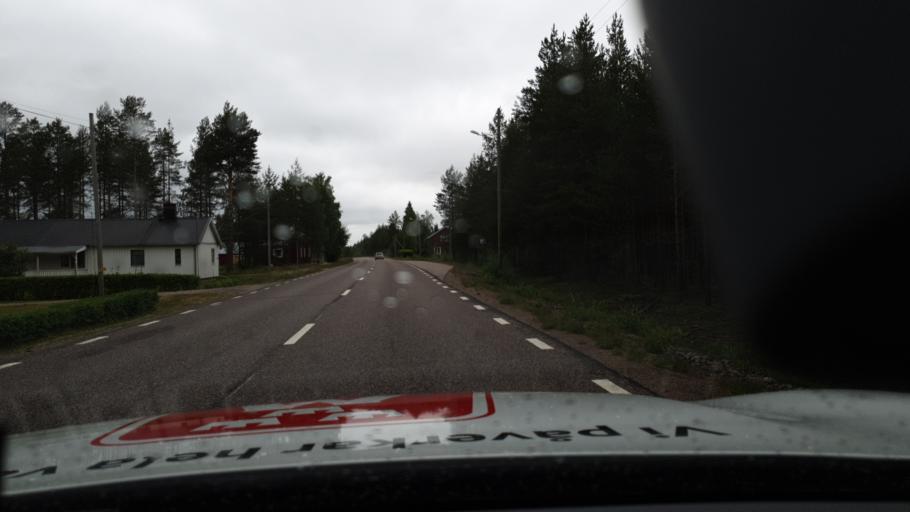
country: FI
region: Lapland
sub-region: Torniolaakso
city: Pello
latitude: 66.9893
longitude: 23.7827
